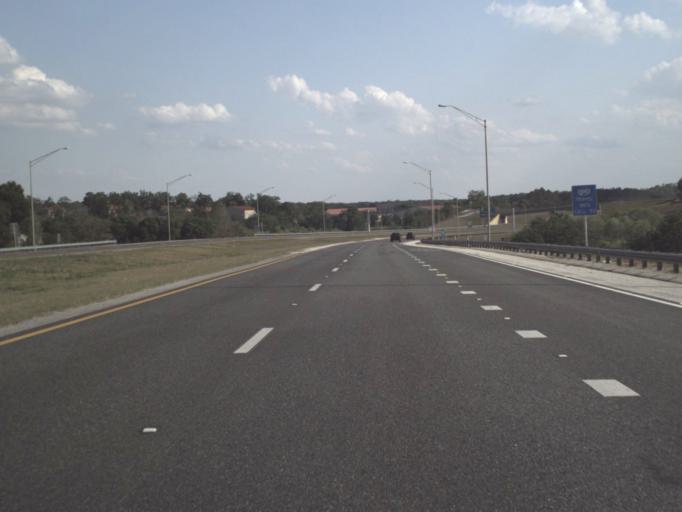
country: US
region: Florida
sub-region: Orange County
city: Apopka
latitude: 28.6760
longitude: -81.5274
